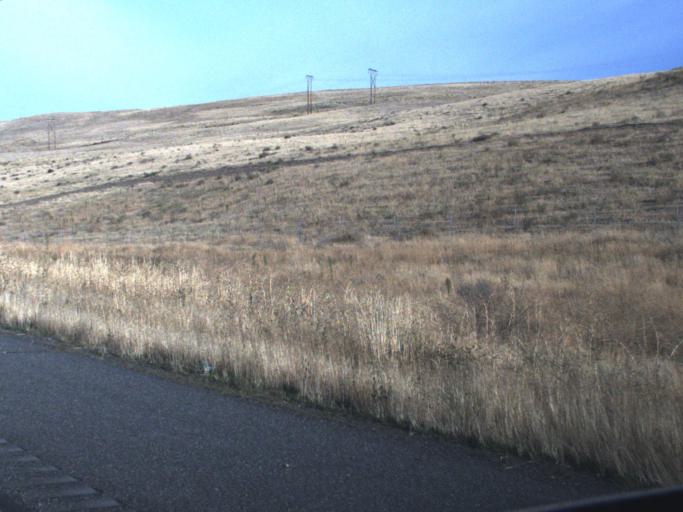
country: US
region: Oregon
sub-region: Umatilla County
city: Umatilla
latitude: 45.9927
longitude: -119.2867
